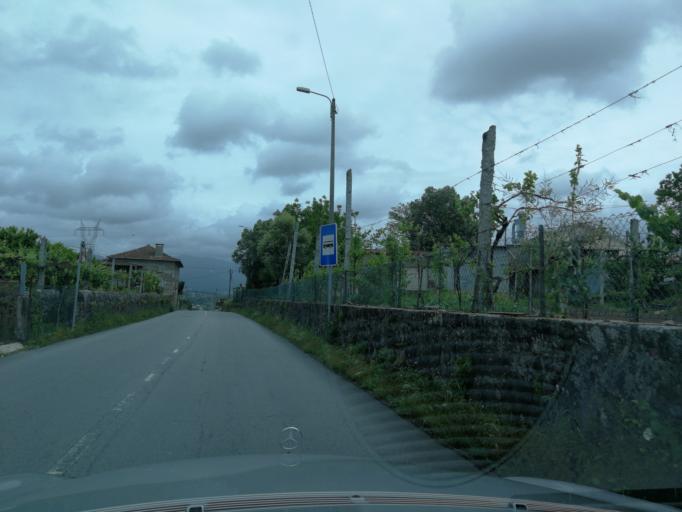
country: PT
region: Braga
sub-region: Amares
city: Amares
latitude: 41.6058
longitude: -8.3559
